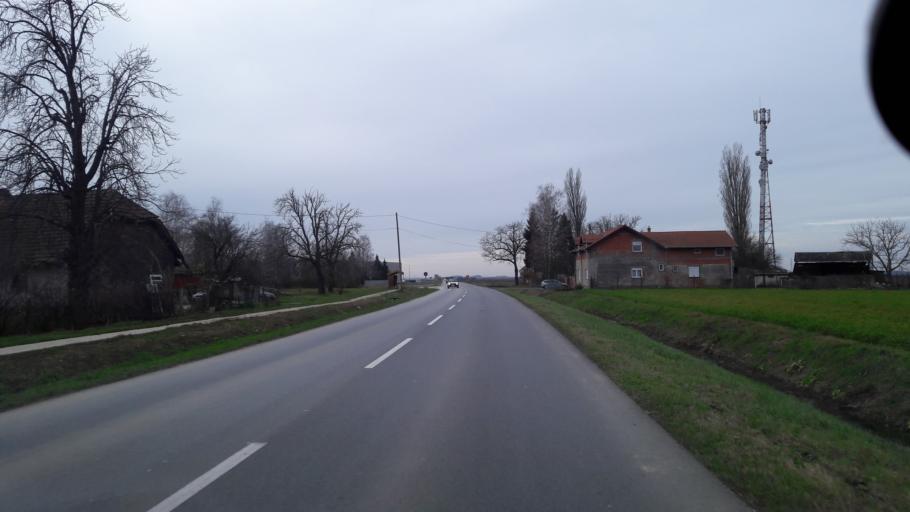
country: HR
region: Osjecko-Baranjska
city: Ovcara
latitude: 45.5046
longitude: 18.5620
